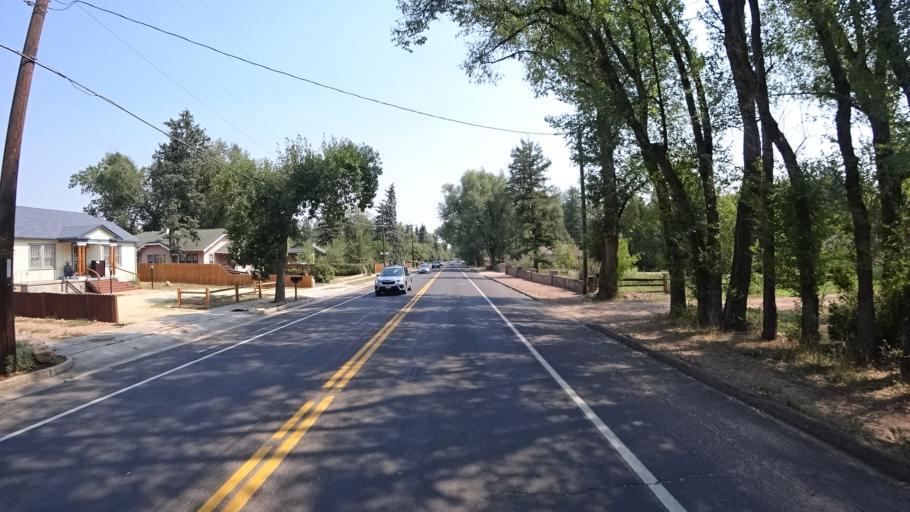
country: US
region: Colorado
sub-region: El Paso County
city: Colorado Springs
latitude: 38.8046
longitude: -104.8336
